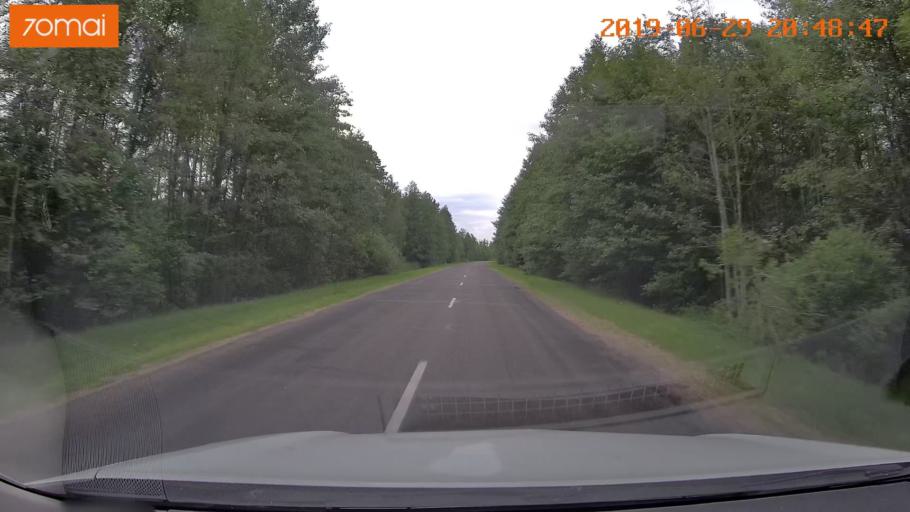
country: BY
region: Brest
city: Hantsavichy
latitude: 52.6551
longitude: 26.3185
